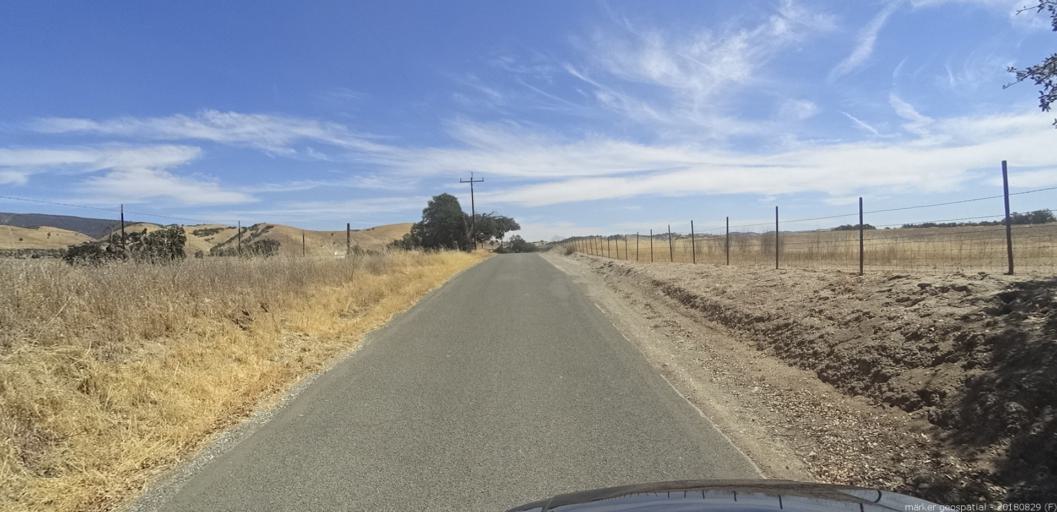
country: US
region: California
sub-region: San Luis Obispo County
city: Lake Nacimiento
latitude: 35.9081
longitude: -121.0364
